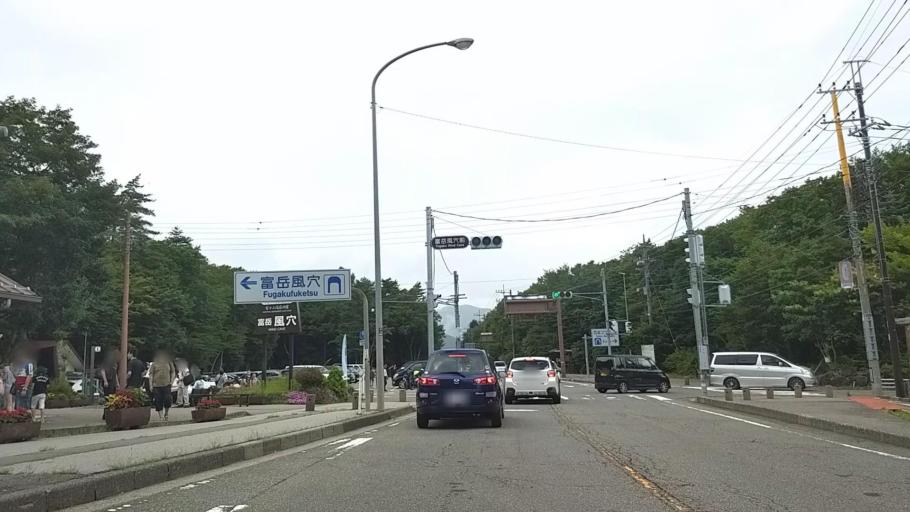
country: JP
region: Yamanashi
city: Fujikawaguchiko
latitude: 35.4792
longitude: 138.6592
